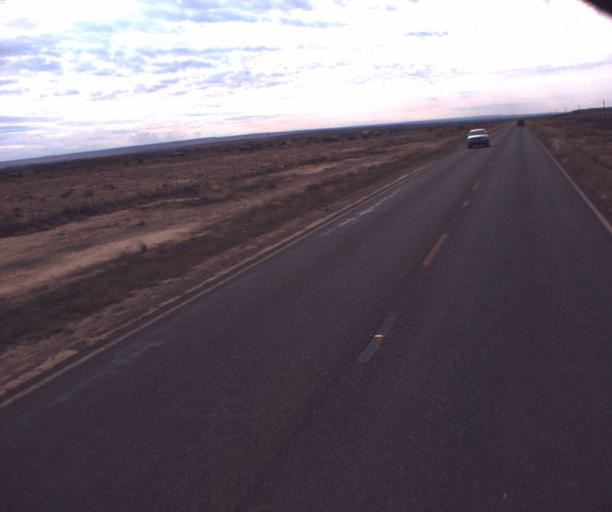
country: US
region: Arizona
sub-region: Apache County
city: Many Farms
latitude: 36.3209
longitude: -109.6165
